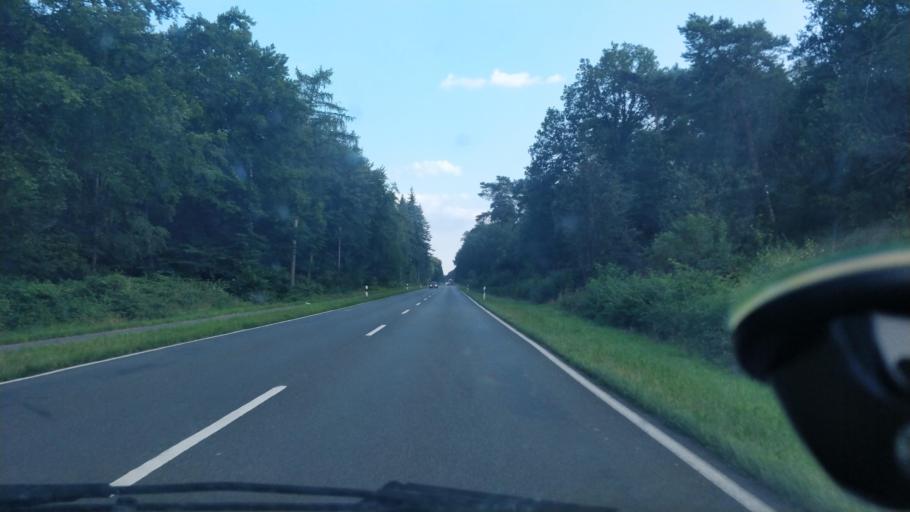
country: DE
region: North Rhine-Westphalia
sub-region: Regierungsbezirk Dusseldorf
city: Alpen
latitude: 51.5493
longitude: 6.5027
